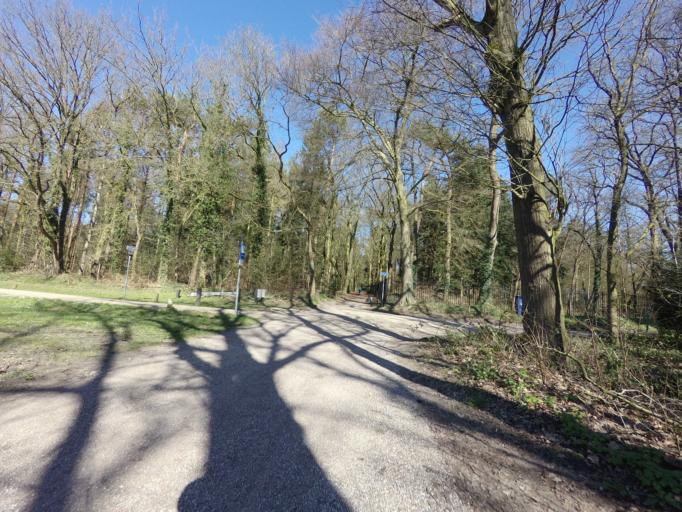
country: NL
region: Utrecht
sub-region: Gemeente Utrechtse Heuvelrug
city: Doorn
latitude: 52.0308
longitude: 5.3267
